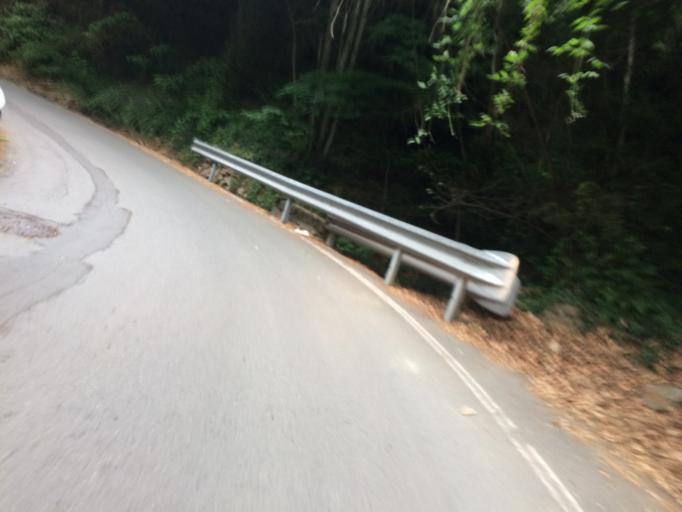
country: IT
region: Liguria
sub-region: Provincia di Imperia
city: Seborga
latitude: 43.8520
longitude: 7.7349
